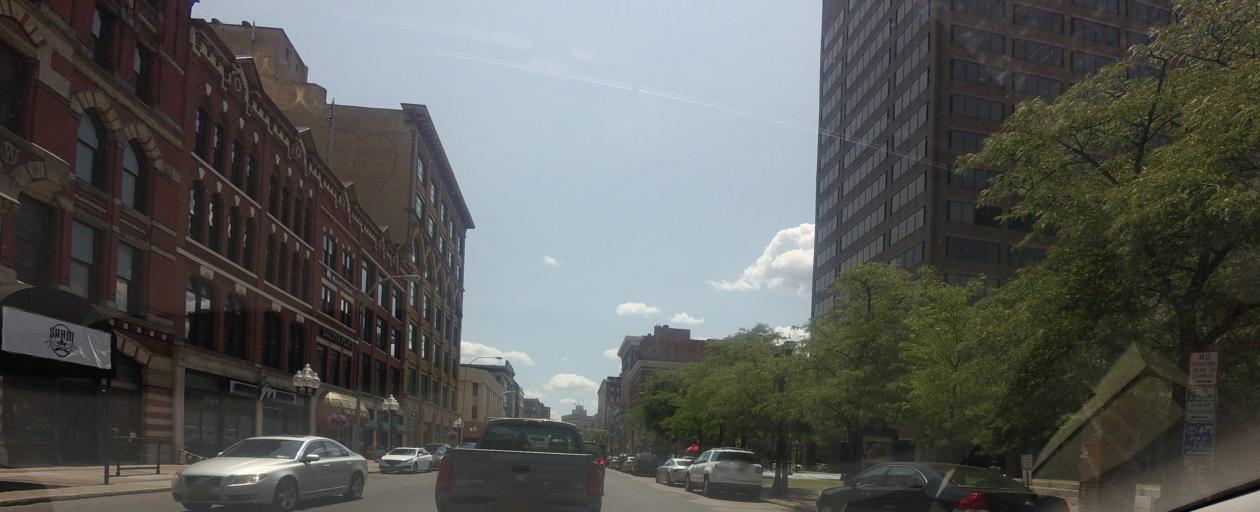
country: US
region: New York
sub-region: Onondaga County
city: Syracuse
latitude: 43.0495
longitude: -76.1522
